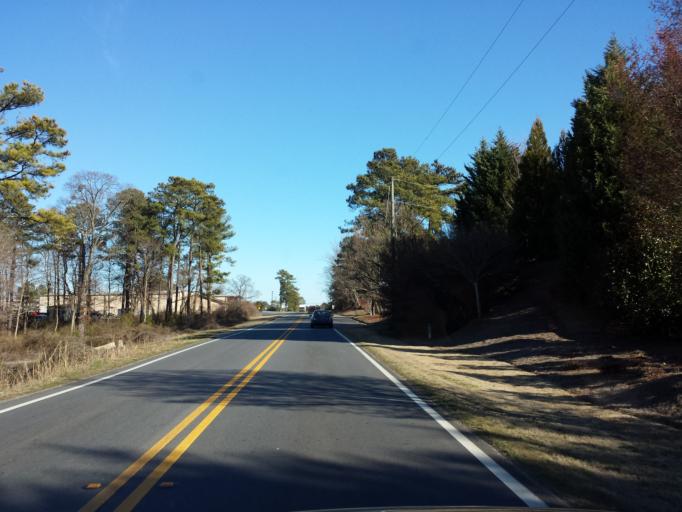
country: US
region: Georgia
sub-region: Cobb County
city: Marietta
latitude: 33.9820
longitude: -84.5687
